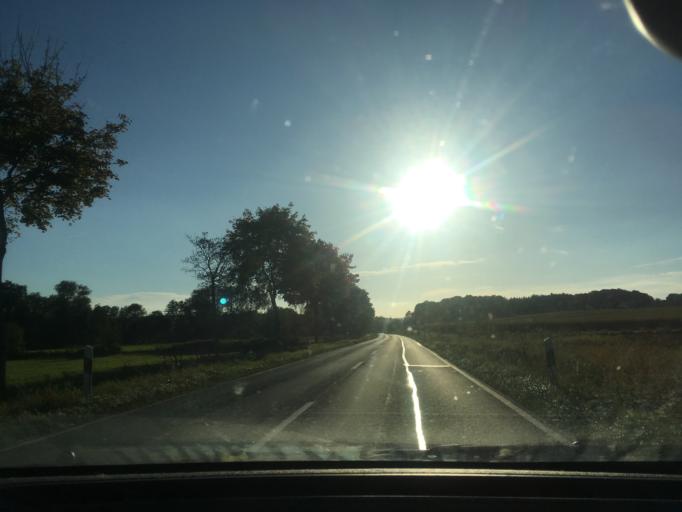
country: DE
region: Lower Saxony
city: Eimen
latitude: 51.8188
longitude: 9.7831
